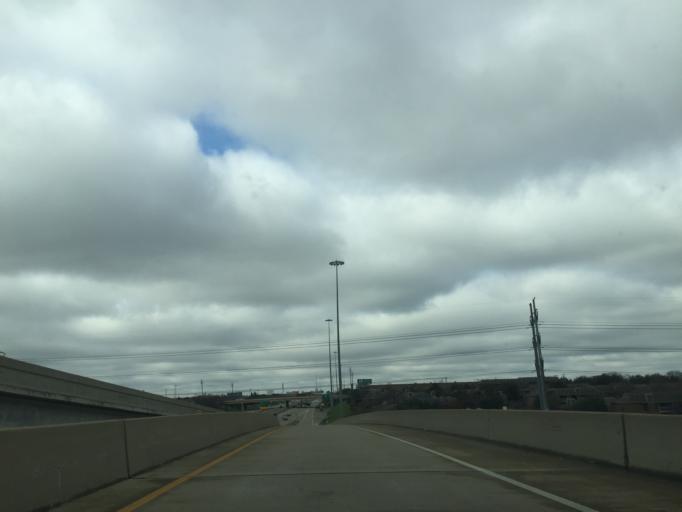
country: US
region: Texas
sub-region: Dallas County
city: Grand Prairie
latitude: 32.7600
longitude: -97.0320
